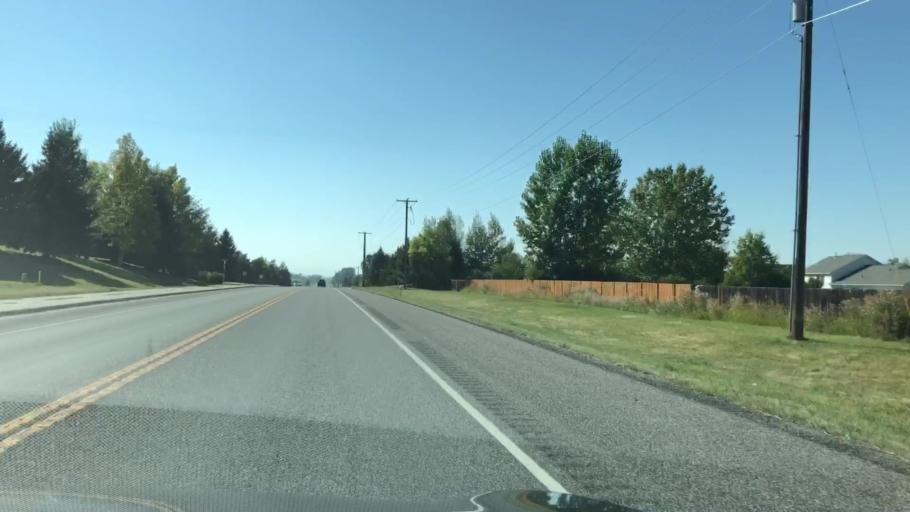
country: US
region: Montana
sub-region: Gallatin County
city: Belgrade
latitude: 45.7293
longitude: -111.1347
